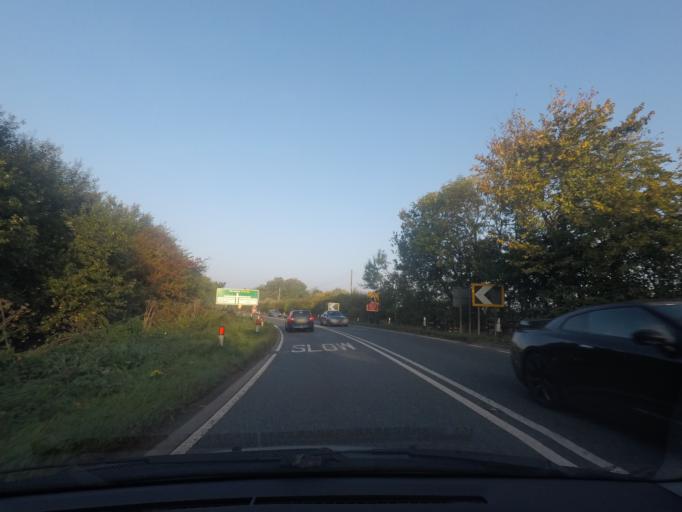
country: GB
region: England
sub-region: City of York
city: Nether Poppleton
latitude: 53.9859
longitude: -1.2165
